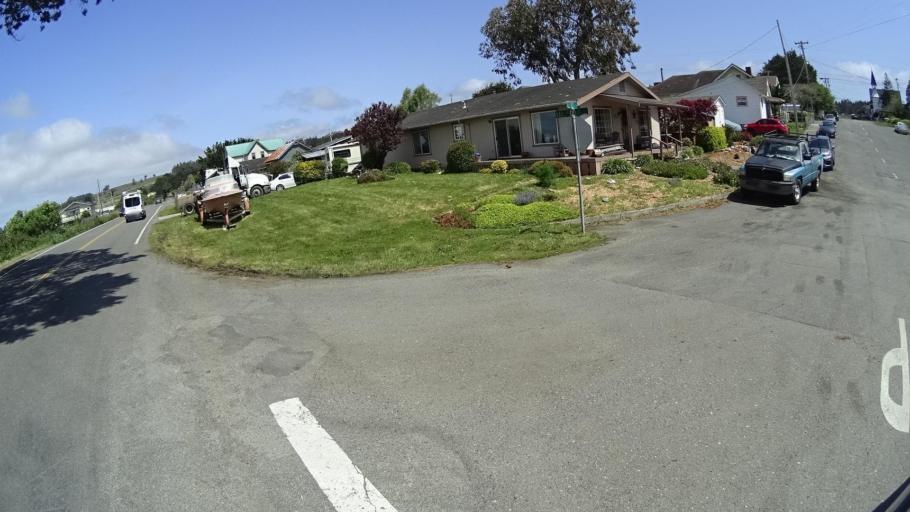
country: US
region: California
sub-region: Humboldt County
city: Ferndale
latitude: 40.6397
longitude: -124.2263
